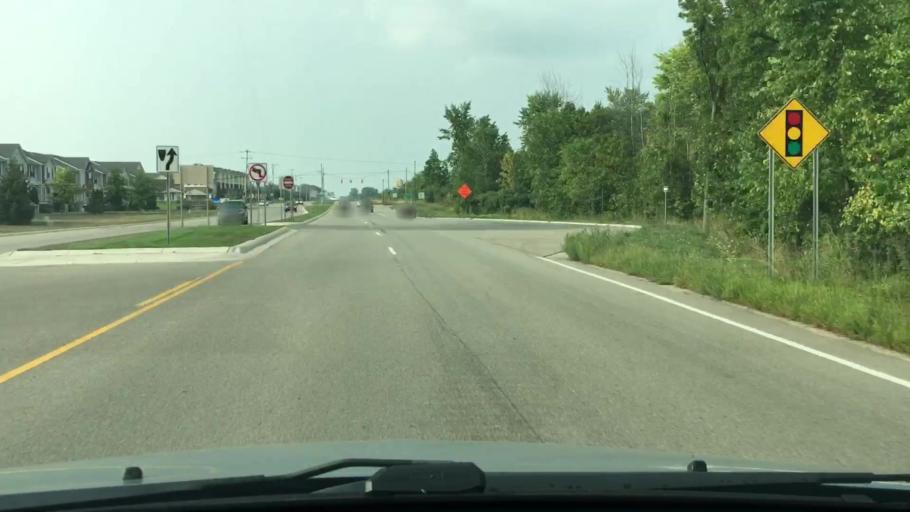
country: US
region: Michigan
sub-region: Ottawa County
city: Allendale
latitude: 42.9558
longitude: -85.9038
